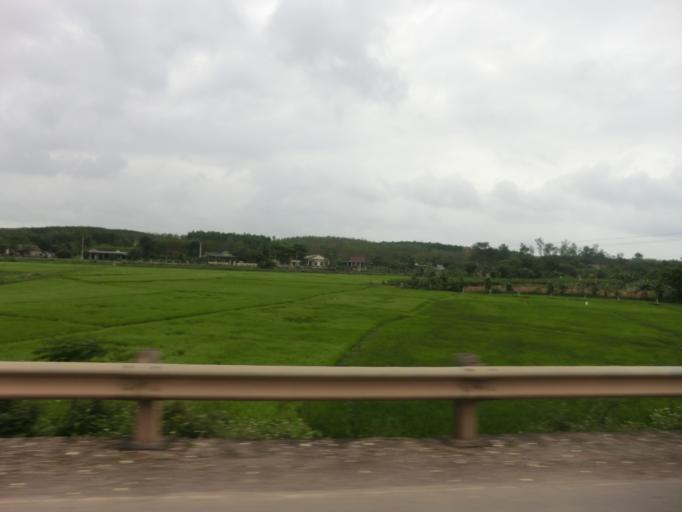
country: VN
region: Quang Tri
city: Cam Lo
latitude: 16.8259
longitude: 107.0089
